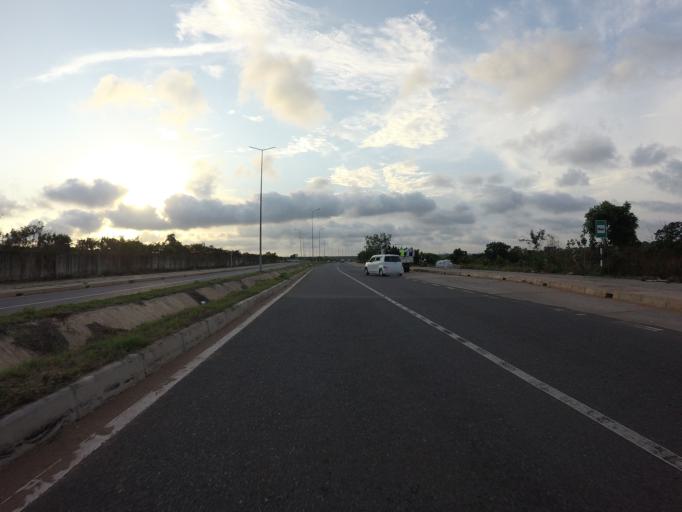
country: GH
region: Greater Accra
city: Teshi Old Town
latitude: 5.6114
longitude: -0.1481
